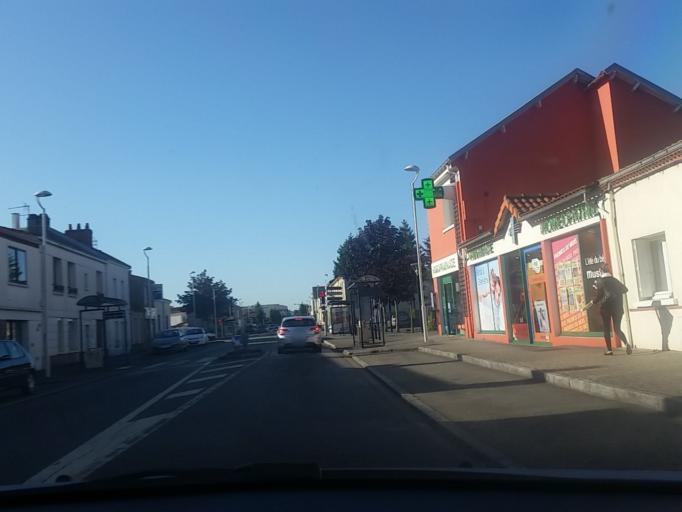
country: FR
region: Pays de la Loire
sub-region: Departement de la Loire-Atlantique
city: Reze
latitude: 47.1790
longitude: -1.5447
